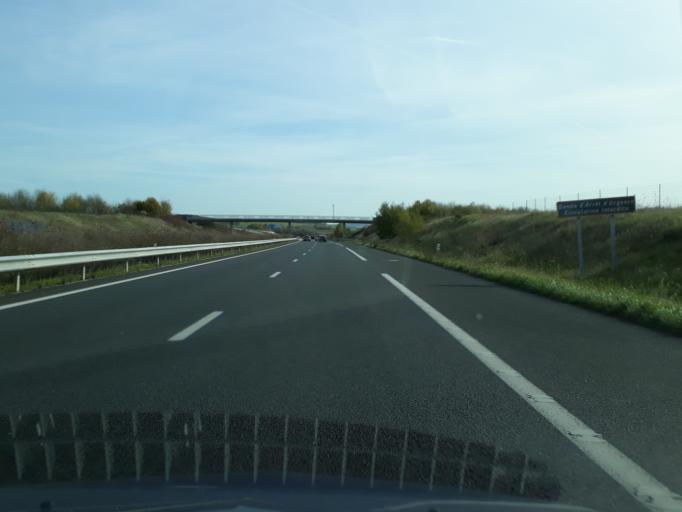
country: FR
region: Champagne-Ardenne
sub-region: Departement de l'Aube
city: Aix-en-Othe
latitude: 48.2410
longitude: 3.5859
